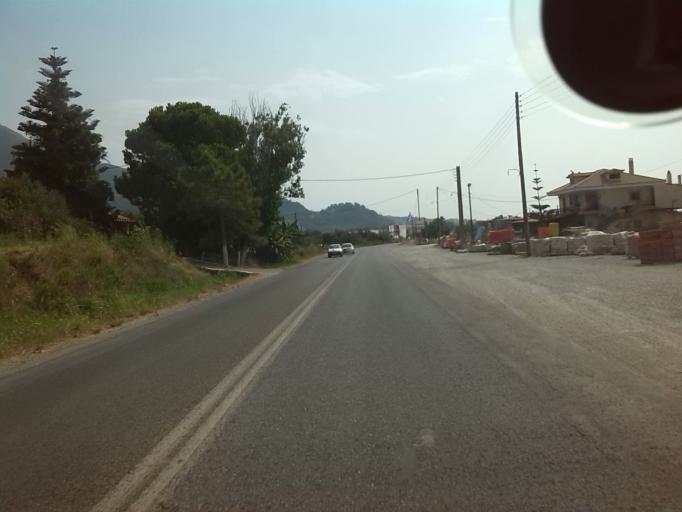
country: GR
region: Peloponnese
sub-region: Nomos Messinias
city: Kyparissia
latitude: 37.2701
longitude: 21.6948
